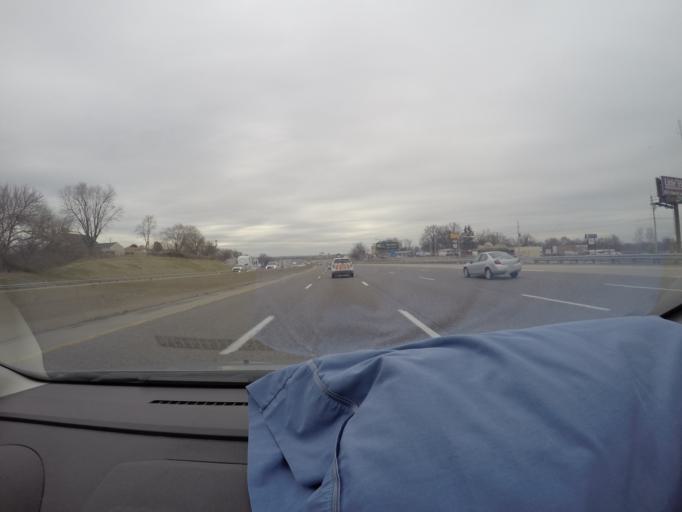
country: US
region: Missouri
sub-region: Saint Charles County
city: Saint Charles
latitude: 38.7742
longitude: -90.5081
